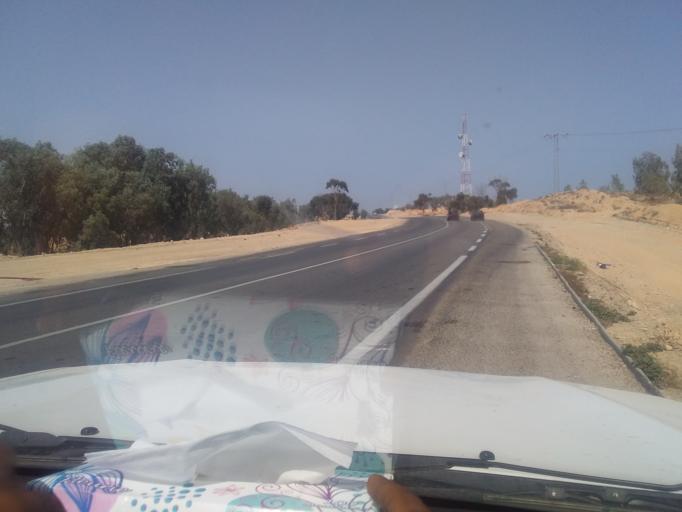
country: TN
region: Madanin
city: Medenine
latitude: 33.5658
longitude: 10.3170
